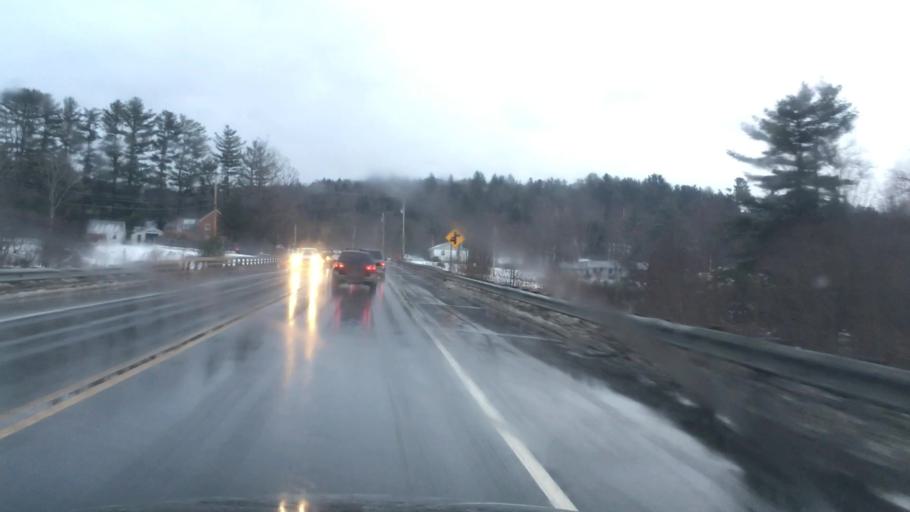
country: US
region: New Hampshire
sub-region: Sullivan County
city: Newport
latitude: 43.3626
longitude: -72.2257
